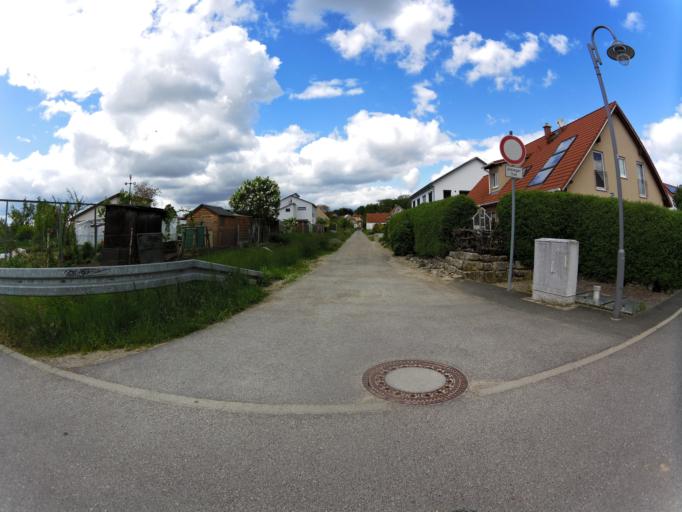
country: DE
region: Bavaria
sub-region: Regierungsbezirk Unterfranken
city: Volkach
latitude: 49.8888
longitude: 10.2303
